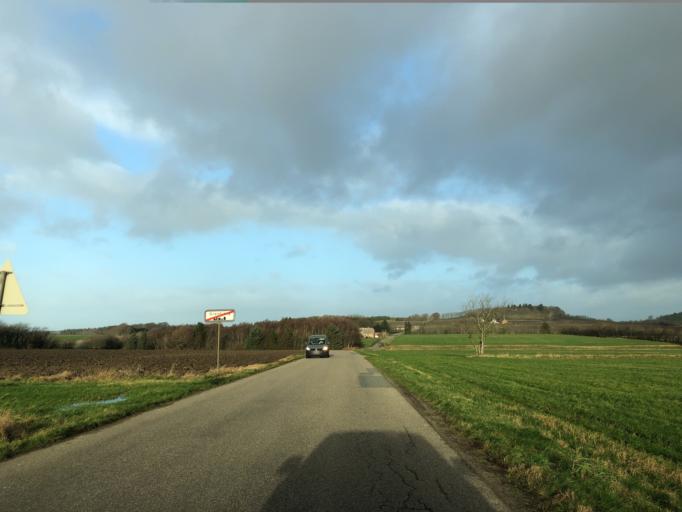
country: DK
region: Central Jutland
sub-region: Ringkobing-Skjern Kommune
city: Videbaek
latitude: 56.1795
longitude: 8.5390
